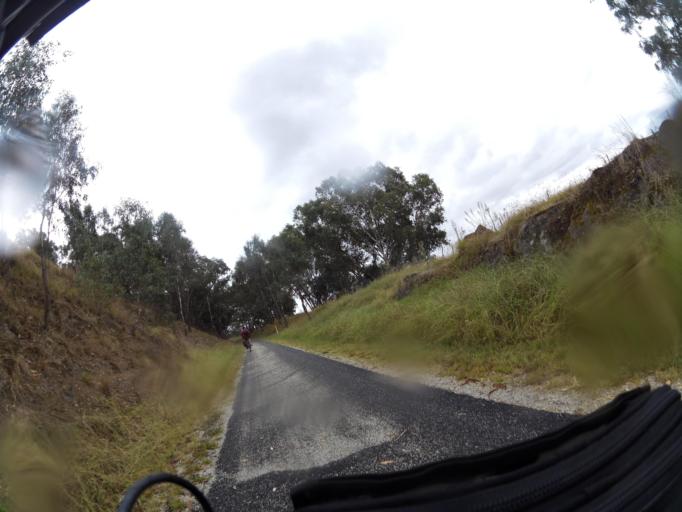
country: AU
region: New South Wales
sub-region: Albury Municipality
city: East Albury
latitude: -36.2145
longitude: 147.2416
